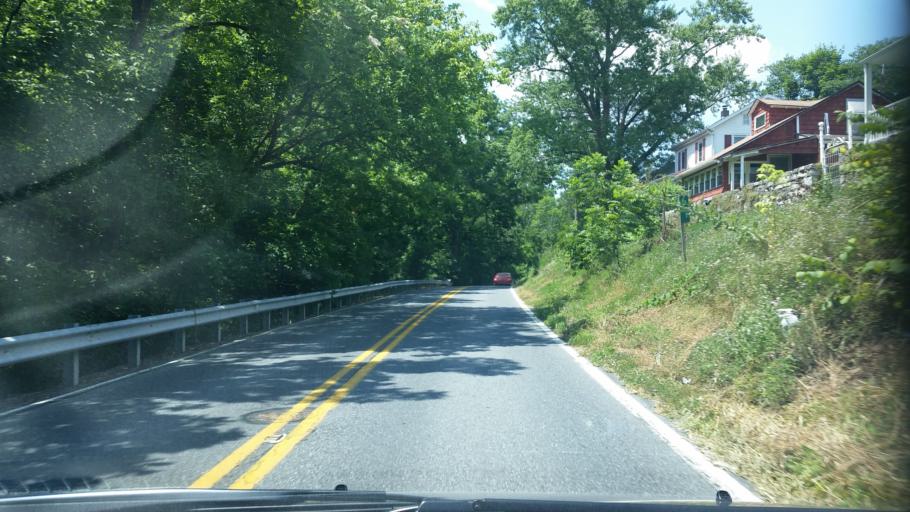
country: US
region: Pennsylvania
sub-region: Dauphin County
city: Hummelstown
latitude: 40.2884
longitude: -76.6854
